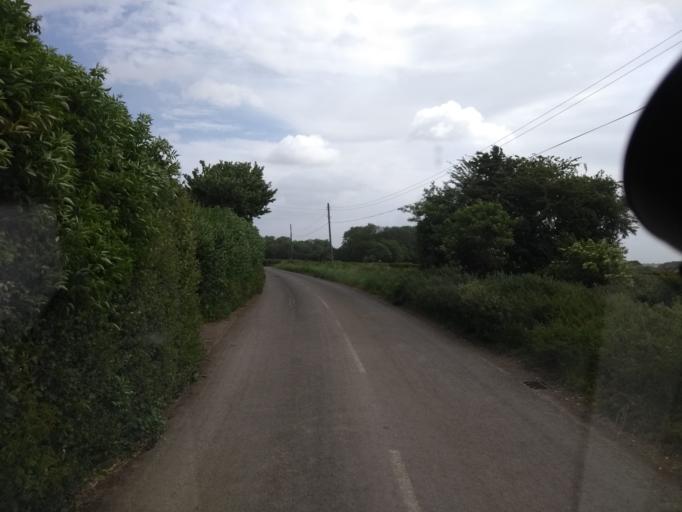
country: GB
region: England
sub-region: Somerset
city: Bishops Lydeard
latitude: 51.1758
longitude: -3.1793
